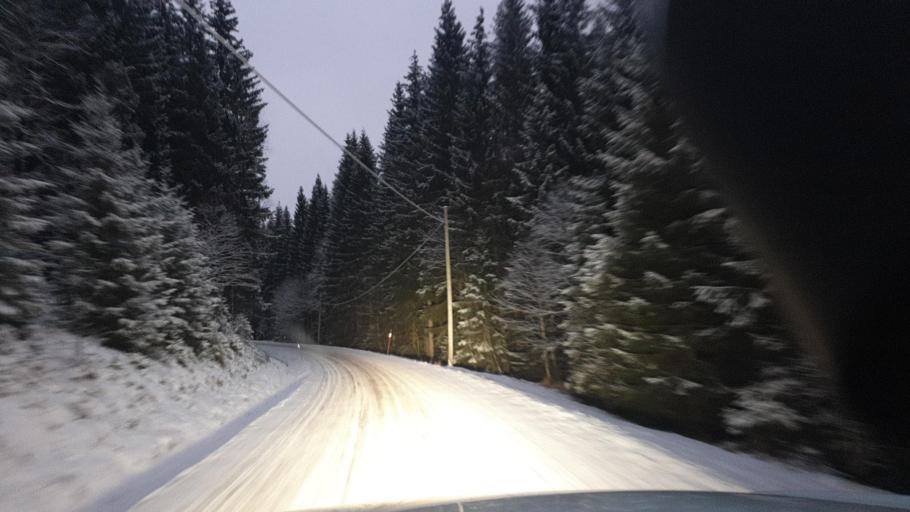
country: SE
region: Vaermland
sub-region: Eda Kommun
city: Charlottenberg
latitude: 59.9283
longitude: 12.3742
